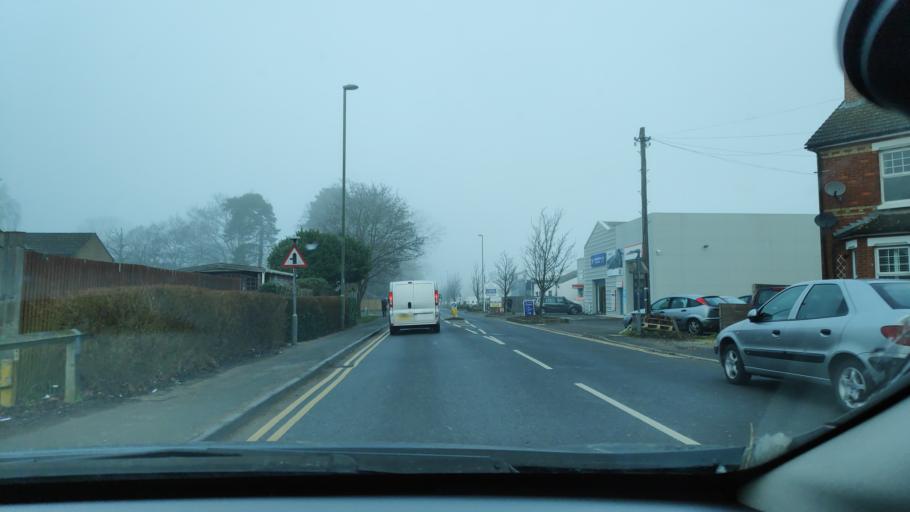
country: GB
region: England
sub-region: Hampshire
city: Farnborough
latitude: 51.2729
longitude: -0.7236
